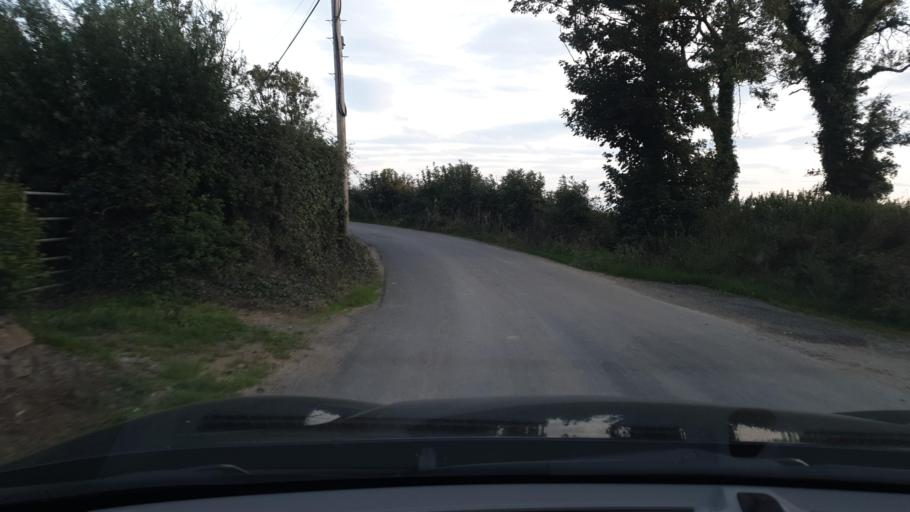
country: IE
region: Leinster
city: Balrothery
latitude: 53.5713
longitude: -6.2427
